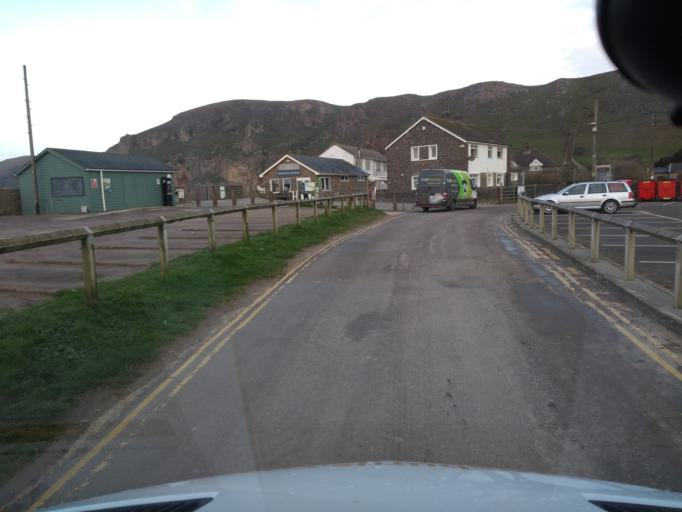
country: GB
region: England
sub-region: North Somerset
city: Weston-super-Mare
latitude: 51.3215
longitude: -3.0107
